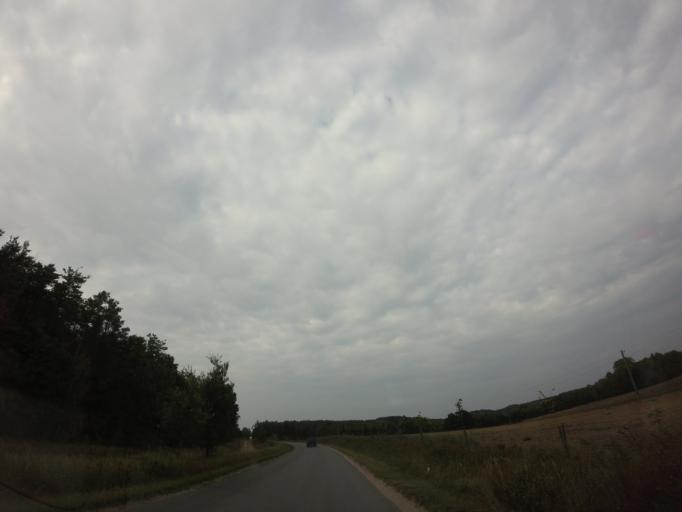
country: PL
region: West Pomeranian Voivodeship
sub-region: Powiat drawski
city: Drawsko Pomorskie
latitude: 53.5016
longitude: 15.7852
